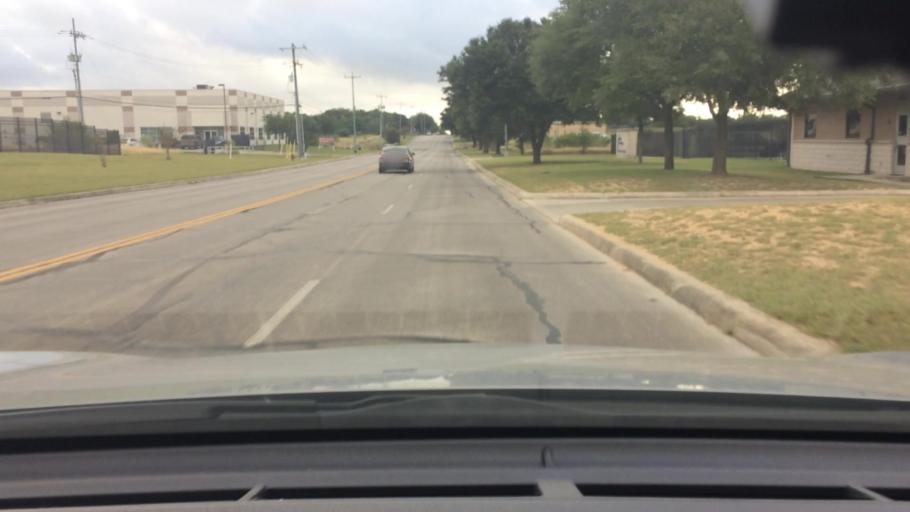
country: US
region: Texas
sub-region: Bexar County
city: Universal City
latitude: 29.5417
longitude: -98.3005
